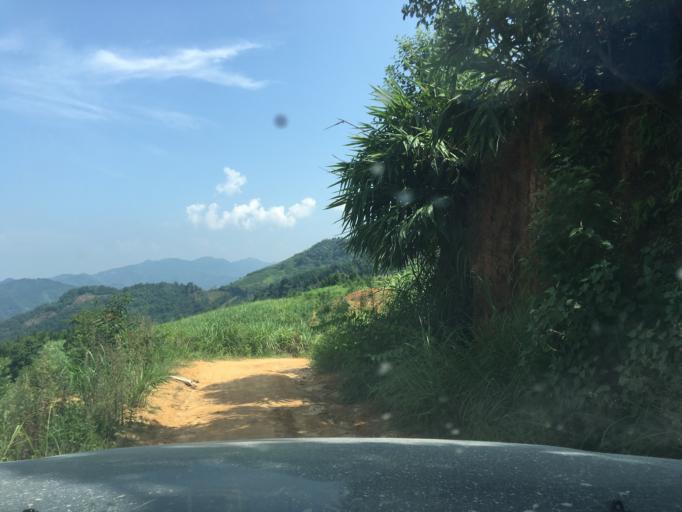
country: CN
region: Guangxi Zhuangzu Zizhiqu
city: Xinzhou
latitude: 25.0455
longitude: 105.8656
